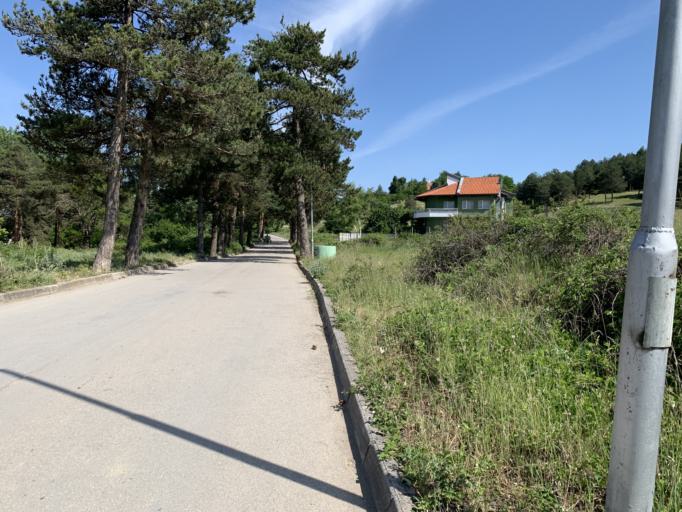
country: AL
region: Korce
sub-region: Rrethi i Korces
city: Korce
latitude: 40.6133
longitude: 20.7898
